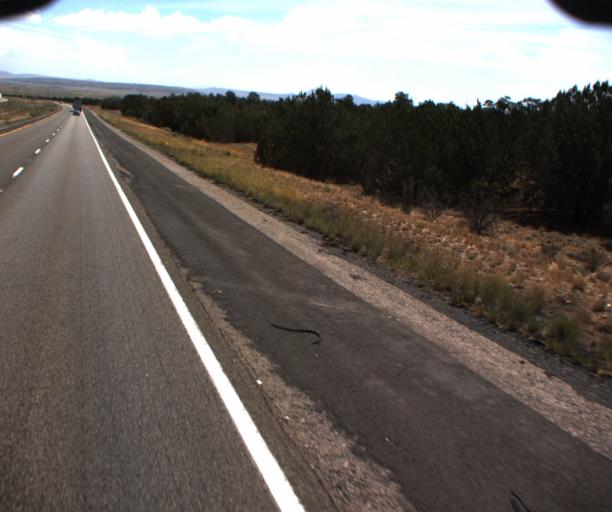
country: US
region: Arizona
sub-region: Mohave County
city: Peach Springs
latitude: 35.3021
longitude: -113.0100
